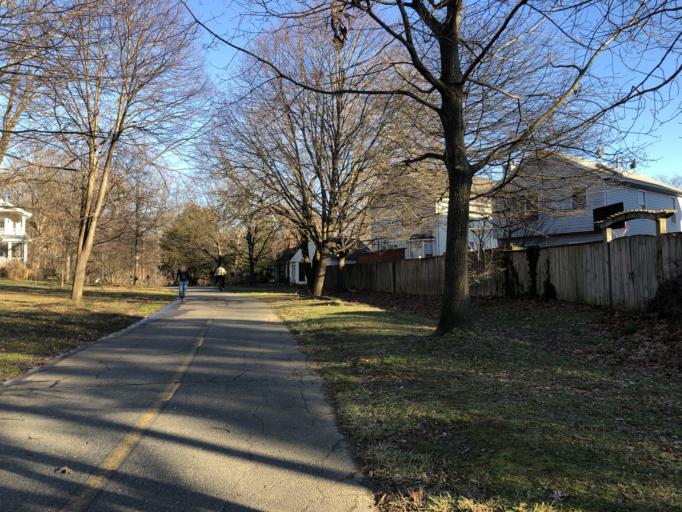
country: US
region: Virginia
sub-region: Fairfax County
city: Baileys Crossroads
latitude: 38.8709
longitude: -77.1294
